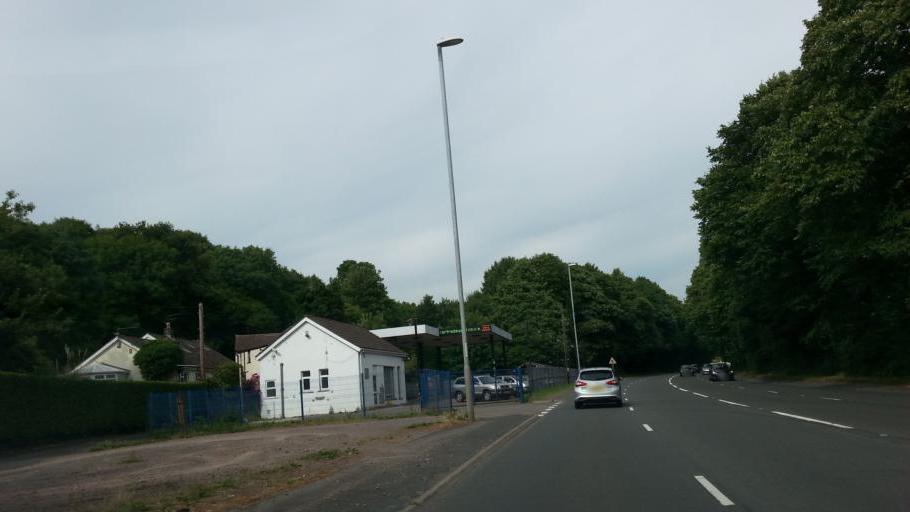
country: GB
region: Wales
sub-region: Newport
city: Marshfield
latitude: 51.5492
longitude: -3.0734
